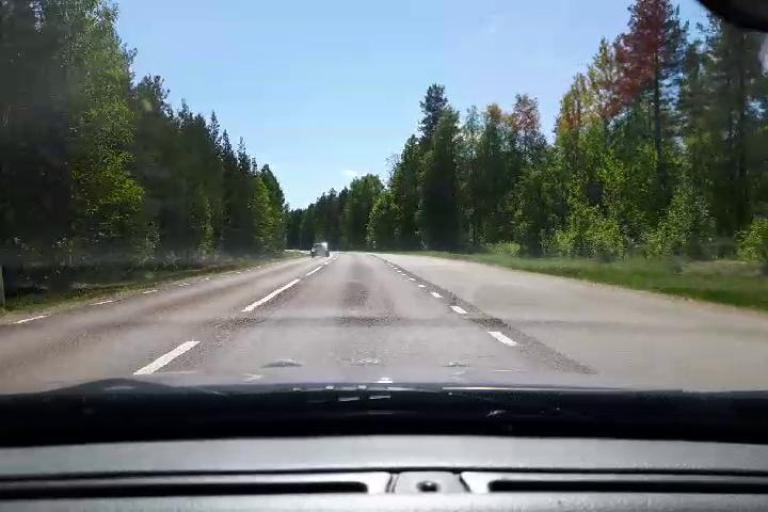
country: SE
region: Jaemtland
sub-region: Harjedalens Kommun
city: Sveg
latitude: 62.1518
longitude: 14.9534
